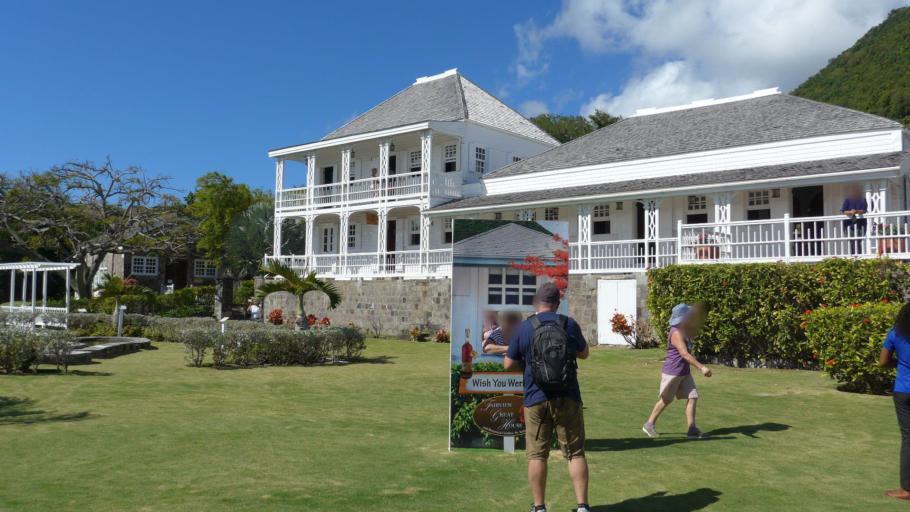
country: KN
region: Trinity Palmetto Point
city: Trinity
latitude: 17.3013
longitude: -62.7707
